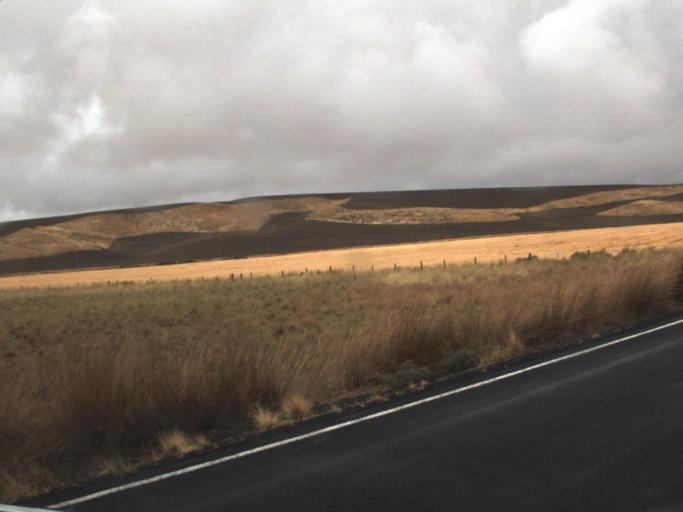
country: US
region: Washington
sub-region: Spokane County
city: Cheney
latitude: 47.1255
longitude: -117.8278
